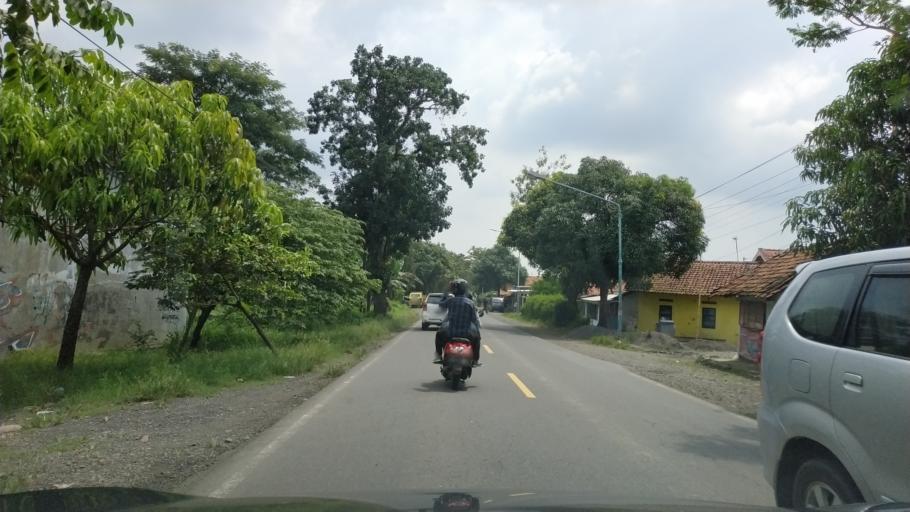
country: ID
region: Central Java
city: Lebaksiu
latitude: -7.0246
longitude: 109.1425
